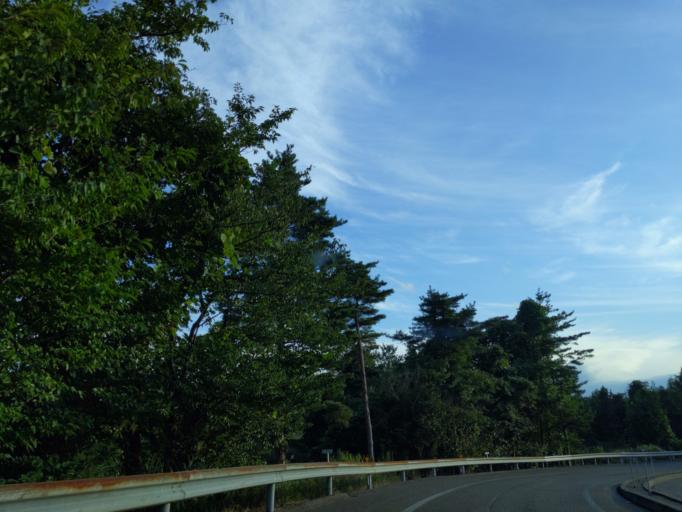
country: JP
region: Niigata
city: Kashiwazaki
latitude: 37.4410
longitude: 138.6605
